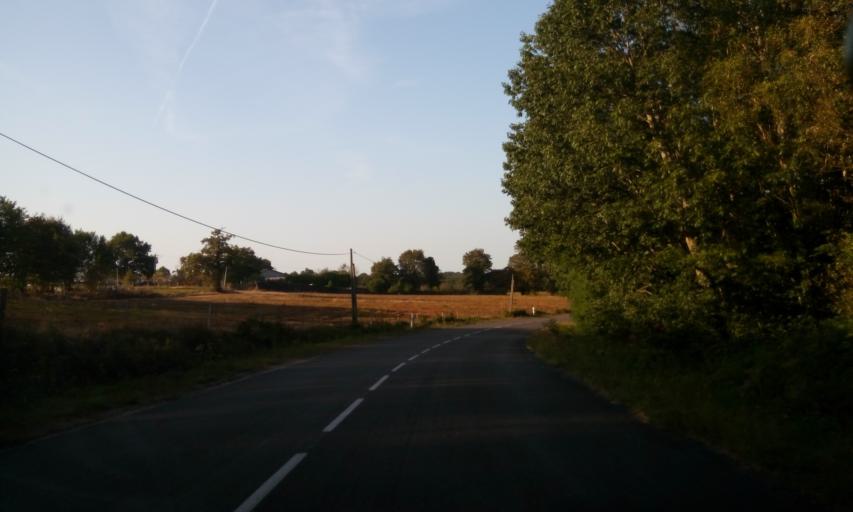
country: FR
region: Rhone-Alpes
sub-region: Departement de l'Ain
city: Chalamont
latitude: 46.0149
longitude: 5.2049
